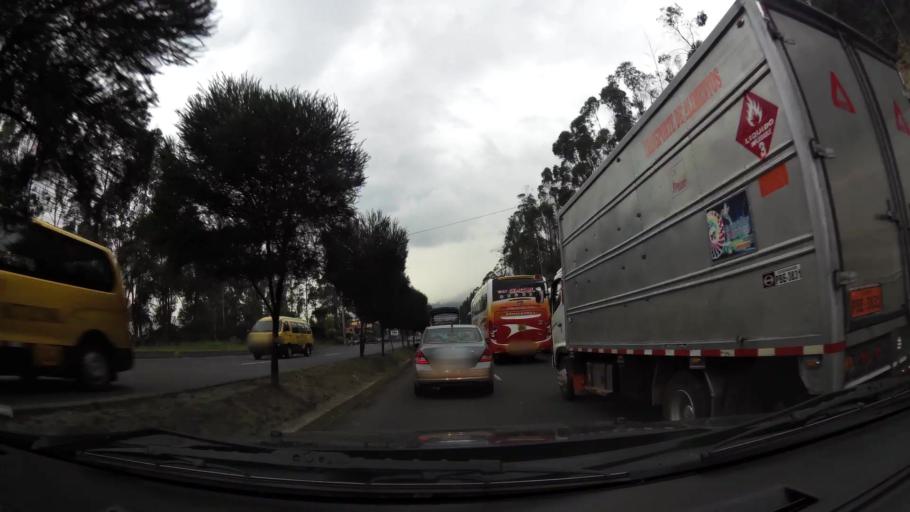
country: EC
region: Pichincha
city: Quito
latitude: -0.1016
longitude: -78.4635
